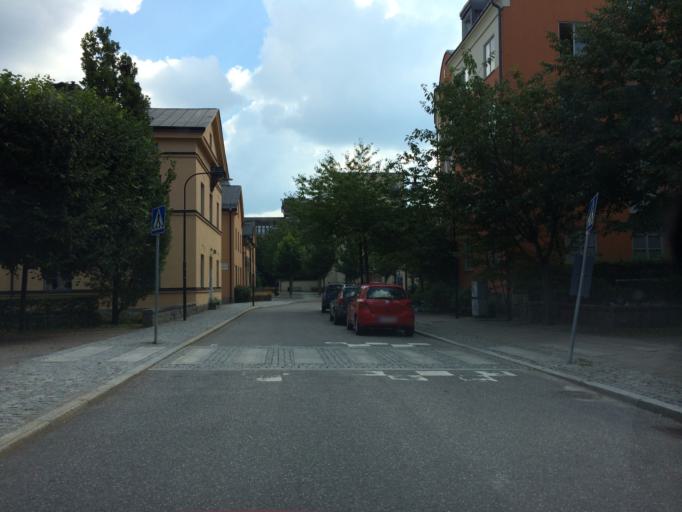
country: SE
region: Stockholm
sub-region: Stockholms Kommun
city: Stockholm
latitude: 59.3347
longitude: 18.0414
